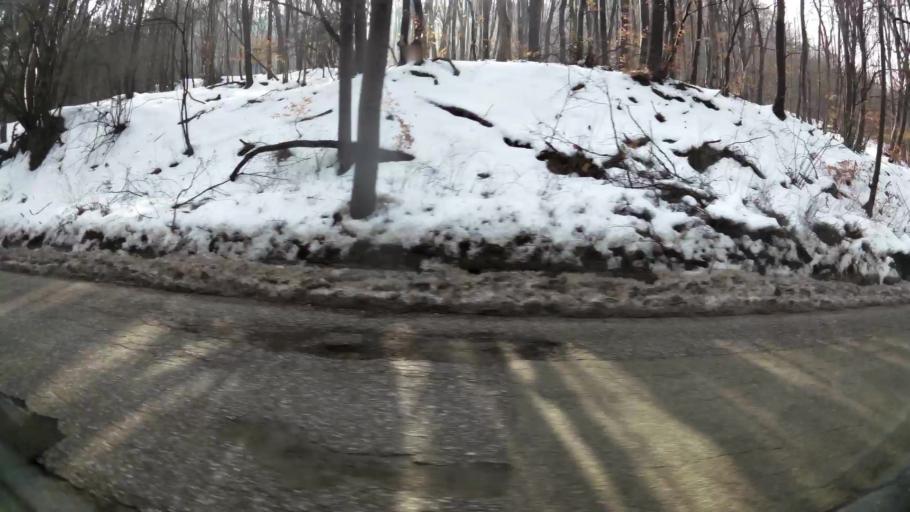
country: BG
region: Sofia-Capital
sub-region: Stolichna Obshtina
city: Sofia
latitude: 42.6461
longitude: 23.2466
